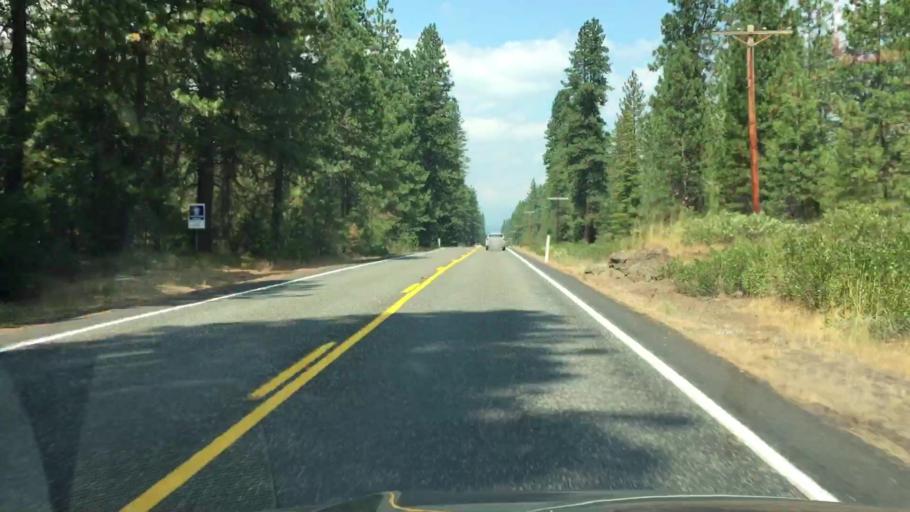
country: US
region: Washington
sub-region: Klickitat County
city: White Salmon
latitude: 45.9791
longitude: -121.5058
